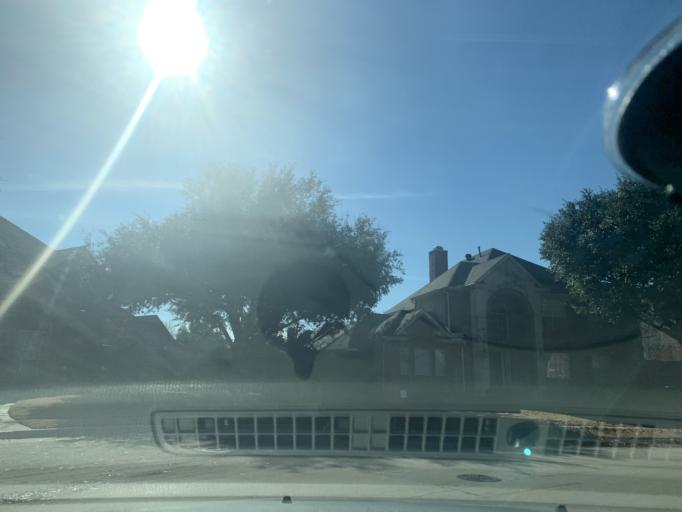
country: US
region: Texas
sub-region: Denton County
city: The Colony
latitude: 33.0527
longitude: -96.8214
